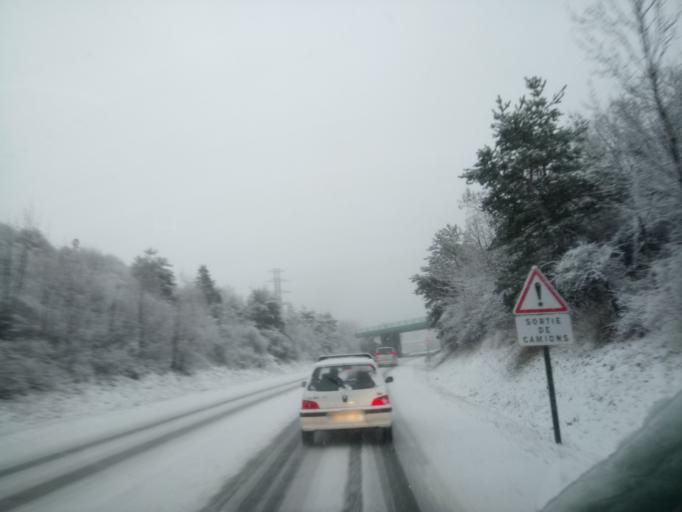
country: FR
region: Rhone-Alpes
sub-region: Departement de la Savoie
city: Saint-Michel-de-Maurienne
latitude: 45.2395
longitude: 6.4358
